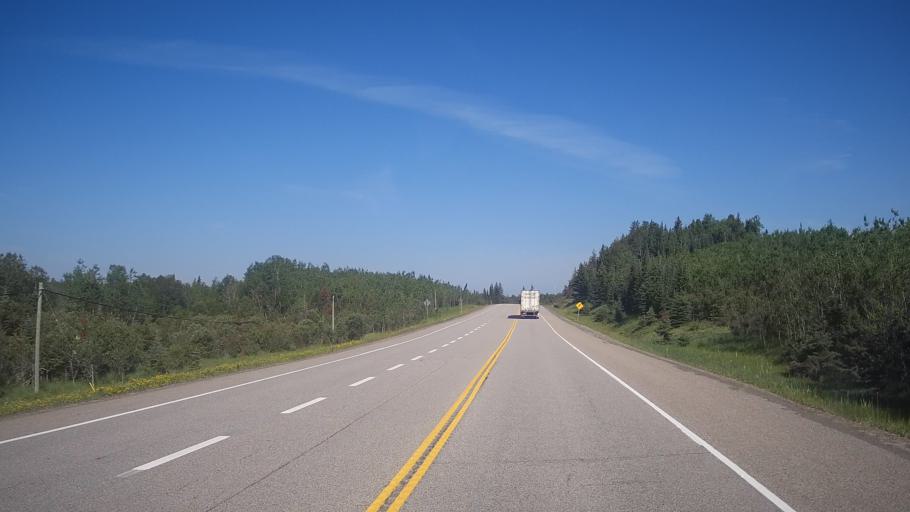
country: CA
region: Ontario
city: Dryden
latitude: 49.7042
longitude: -92.5792
